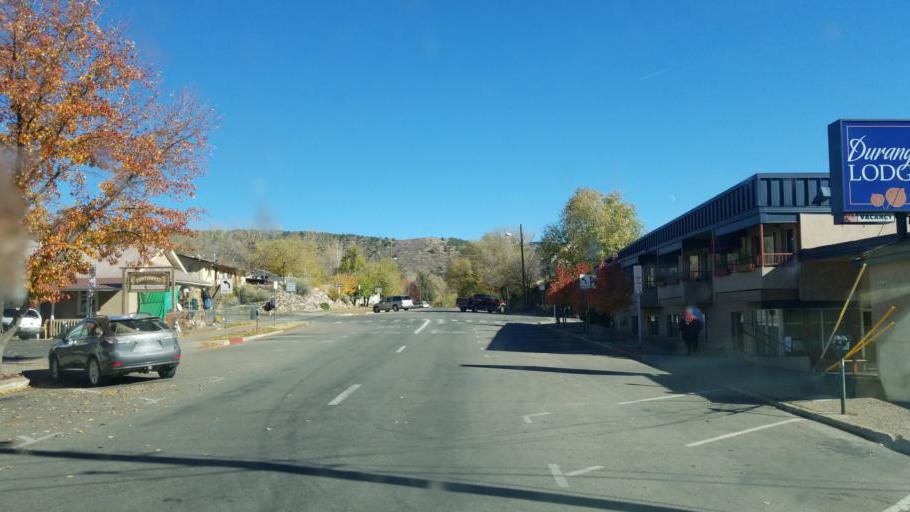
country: US
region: Colorado
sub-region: La Plata County
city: Durango
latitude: 37.2690
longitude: -107.8815
